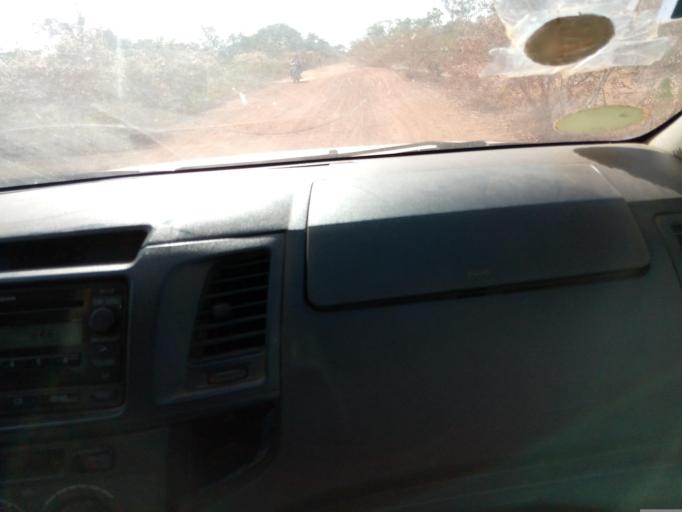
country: ML
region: Sikasso
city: Sikasso
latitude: 11.8788
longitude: -6.0375
